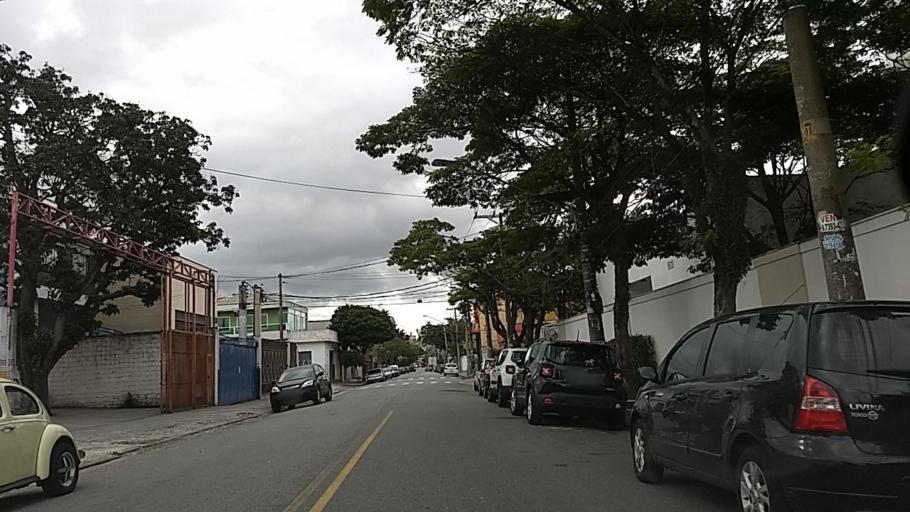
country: BR
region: Sao Paulo
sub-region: Sao Paulo
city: Sao Paulo
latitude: -23.5168
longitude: -46.6112
